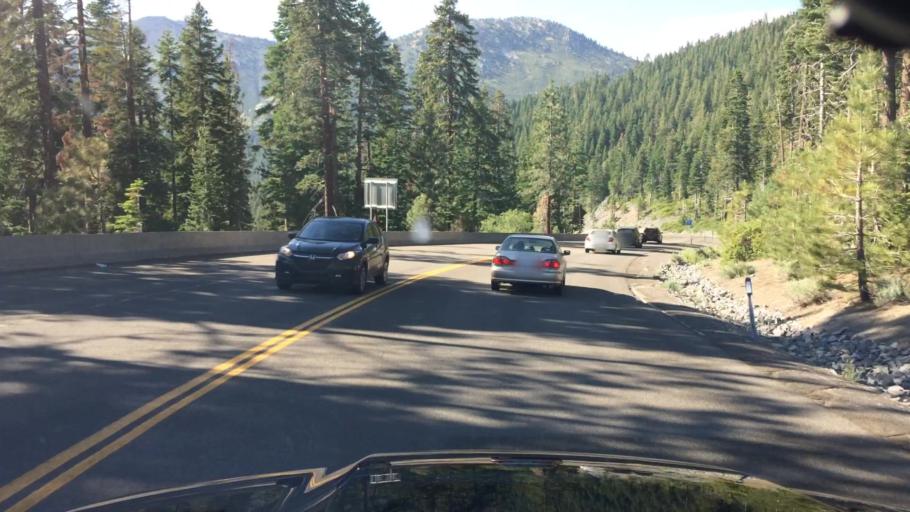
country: US
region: Nevada
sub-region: Washoe County
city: Incline Village
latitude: 39.2634
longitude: -119.9319
